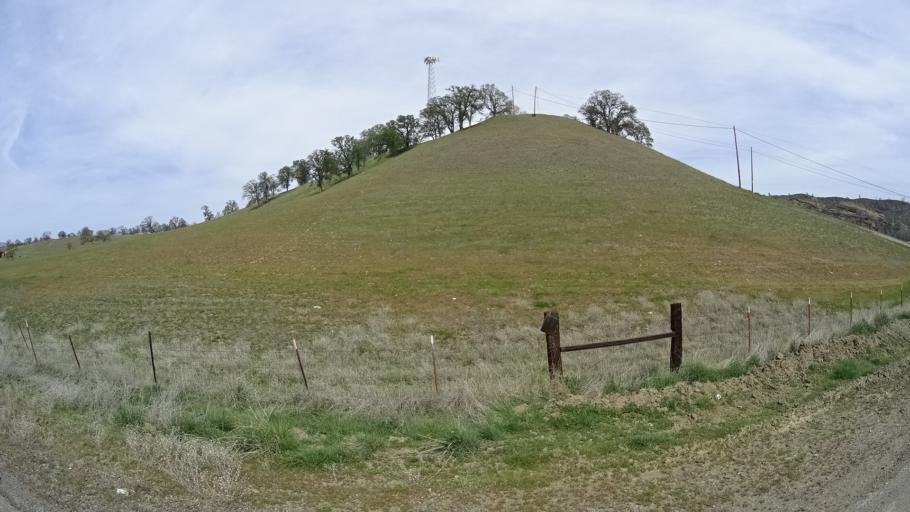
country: US
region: California
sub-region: Glenn County
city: Willows
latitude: 39.5946
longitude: -122.5480
